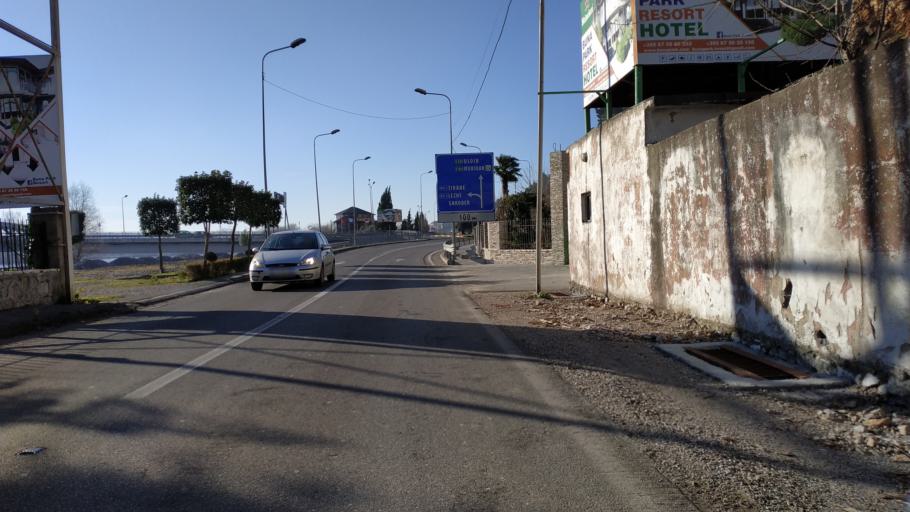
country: AL
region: Shkoder
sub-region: Rrethi i Shkodres
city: Berdica e Madhe
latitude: 42.0471
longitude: 19.4863
